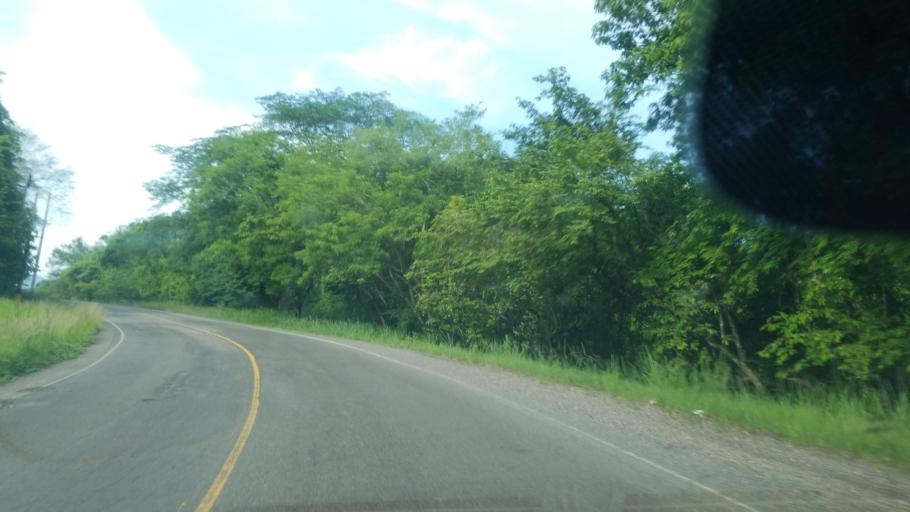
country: HN
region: Santa Barbara
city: Trinidad
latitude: 15.1311
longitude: -88.2512
